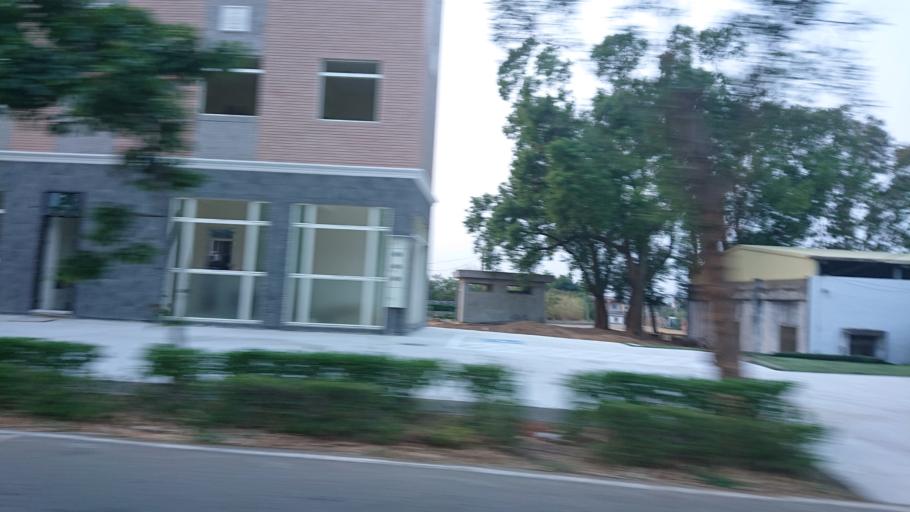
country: TW
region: Fukien
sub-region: Kinmen
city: Jincheng
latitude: 24.4606
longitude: 118.3246
